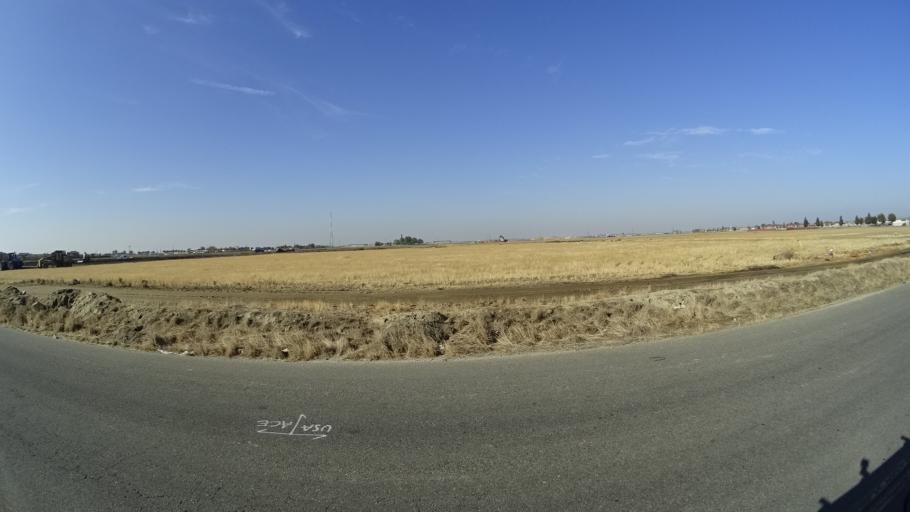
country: US
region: California
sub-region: Kern County
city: Greenfield
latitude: 35.2843
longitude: -119.0655
